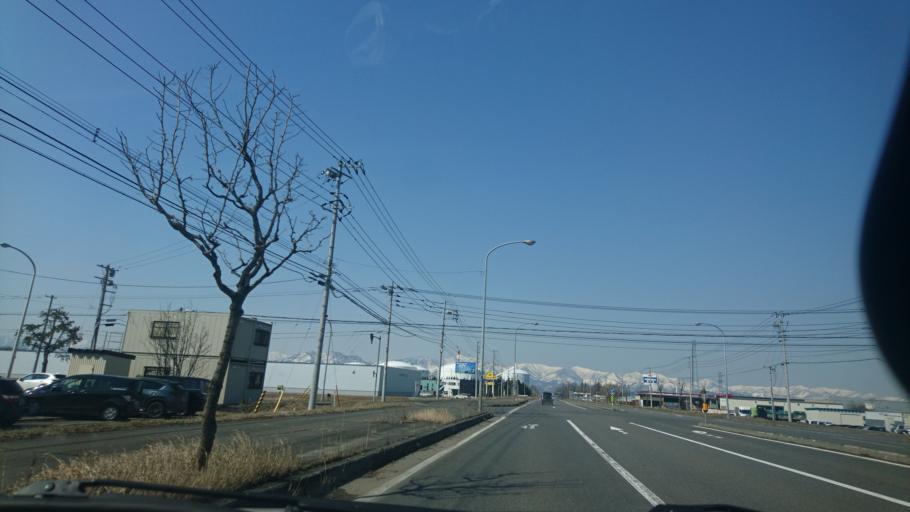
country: JP
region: Hokkaido
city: Obihiro
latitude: 42.9237
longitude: 143.0897
